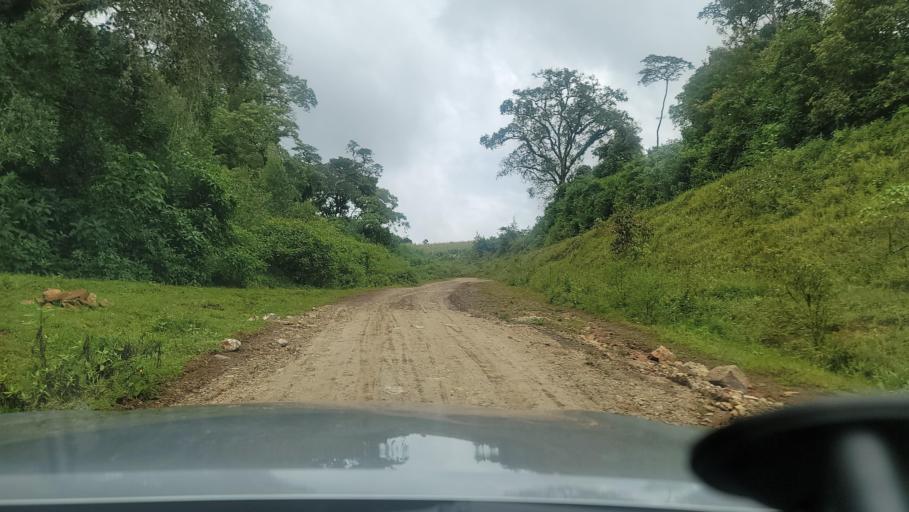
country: ET
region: Southern Nations, Nationalities, and People's Region
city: Bonga
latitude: 7.6370
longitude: 36.2245
